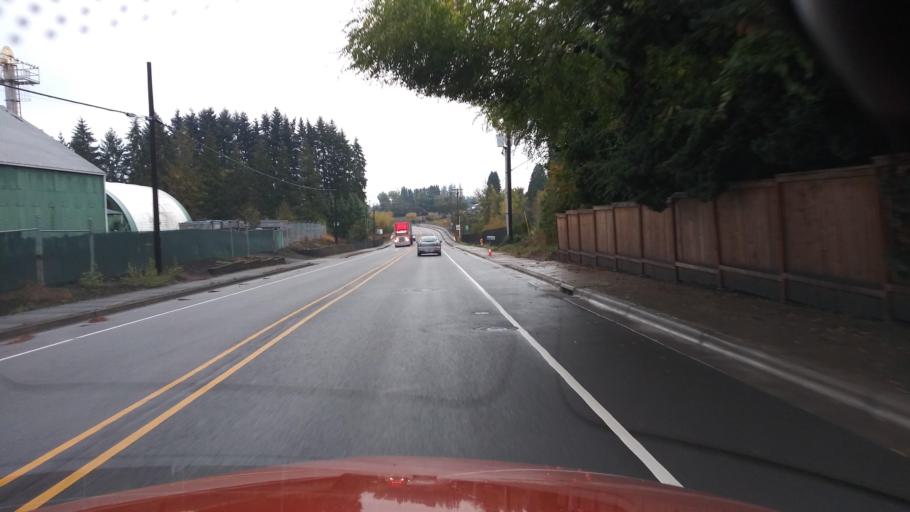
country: US
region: Oregon
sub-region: Washington County
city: Cornelius
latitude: 45.5268
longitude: -123.0592
